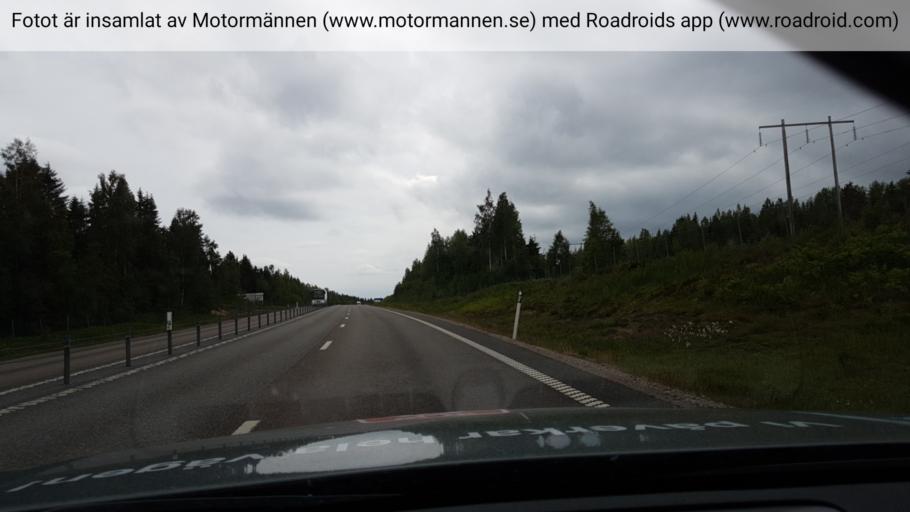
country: SE
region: Vaesternorrland
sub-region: Sundsvalls Kommun
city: Njurundabommen
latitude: 62.1836
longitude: 17.3561
